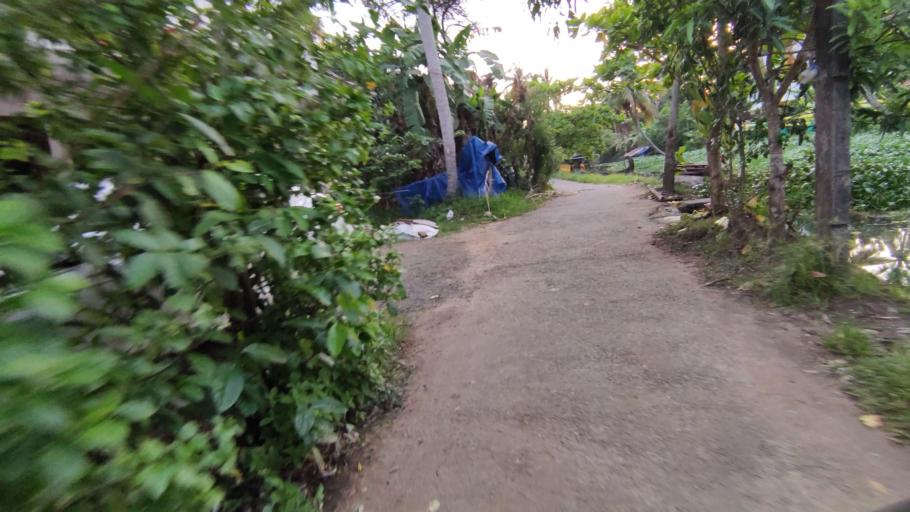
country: IN
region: Kerala
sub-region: Kottayam
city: Kottayam
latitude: 9.5770
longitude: 76.4366
